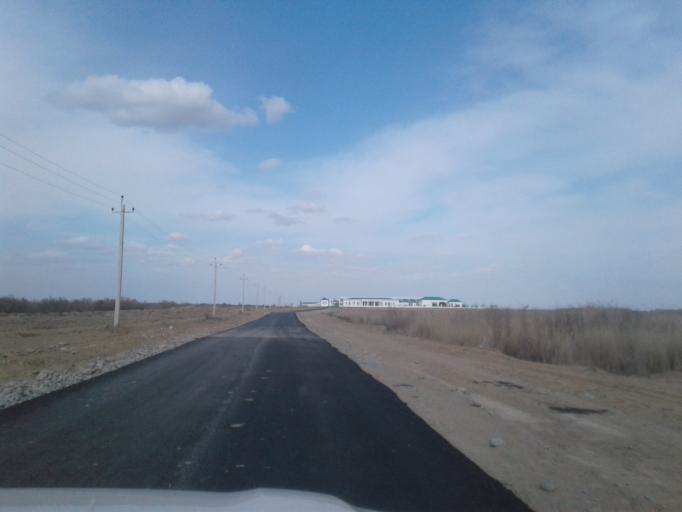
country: TM
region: Ahal
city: Ashgabat
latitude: 38.1922
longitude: 58.4175
